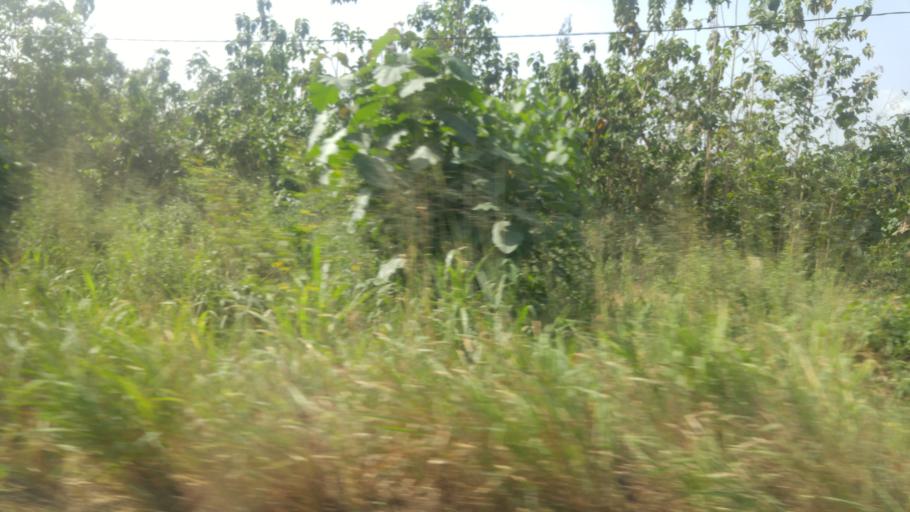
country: BJ
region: Zou
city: Bohicon
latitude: 7.0230
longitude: 2.1769
